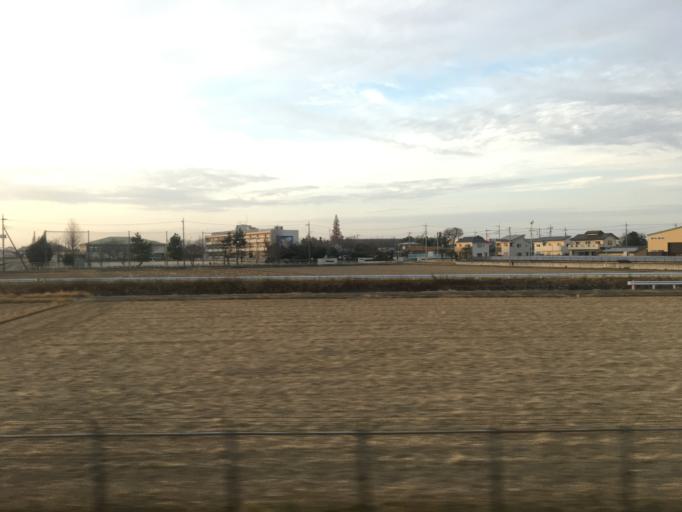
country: JP
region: Saitama
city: Kurihashi
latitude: 36.1178
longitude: 139.6851
